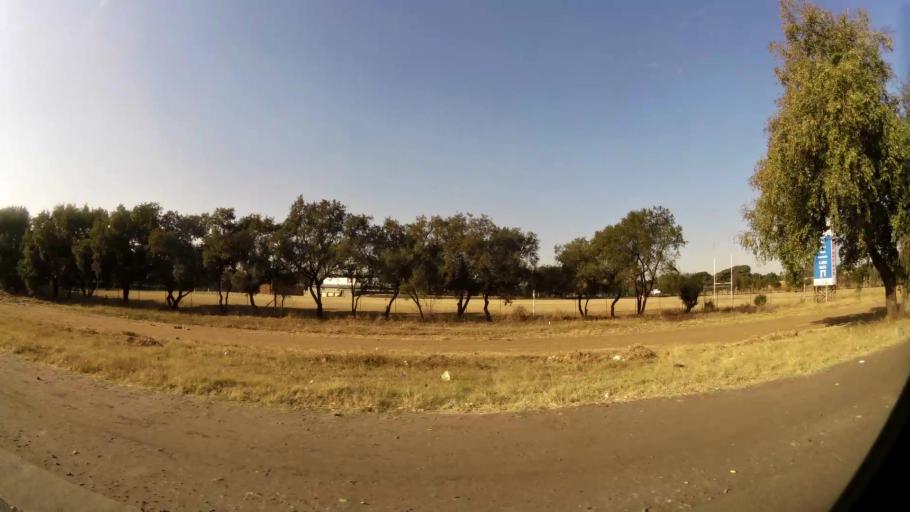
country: ZA
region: North-West
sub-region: Bojanala Platinum District Municipality
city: Rustenburg
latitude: -25.6541
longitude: 27.2428
